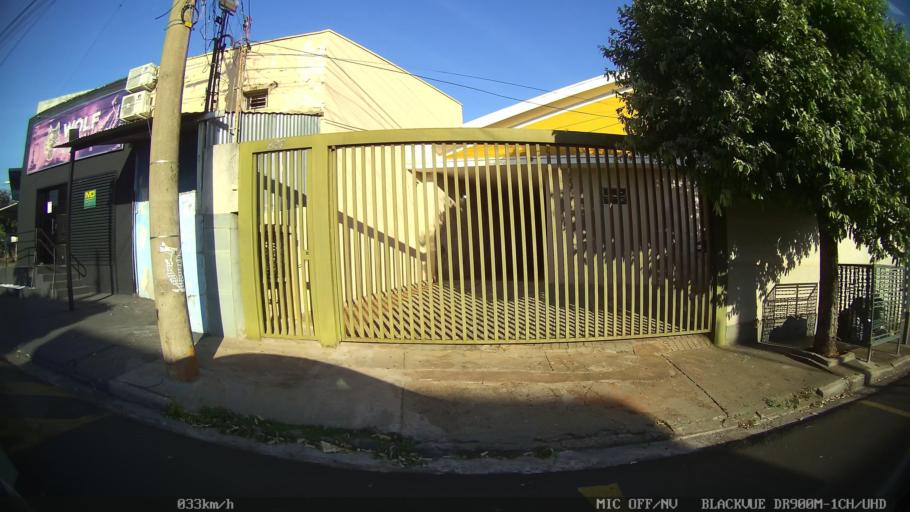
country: BR
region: Sao Paulo
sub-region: Sao Jose Do Rio Preto
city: Sao Jose do Rio Preto
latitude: -20.7997
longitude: -49.3647
